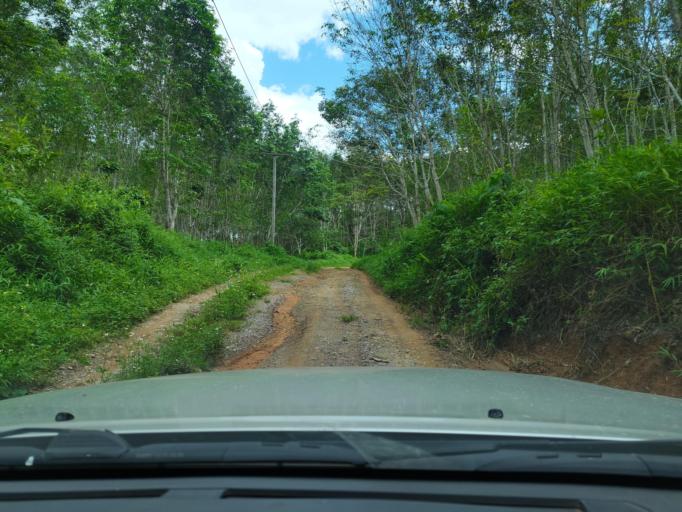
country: LA
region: Loungnamtha
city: Muang Long
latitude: 20.6961
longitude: 101.0392
